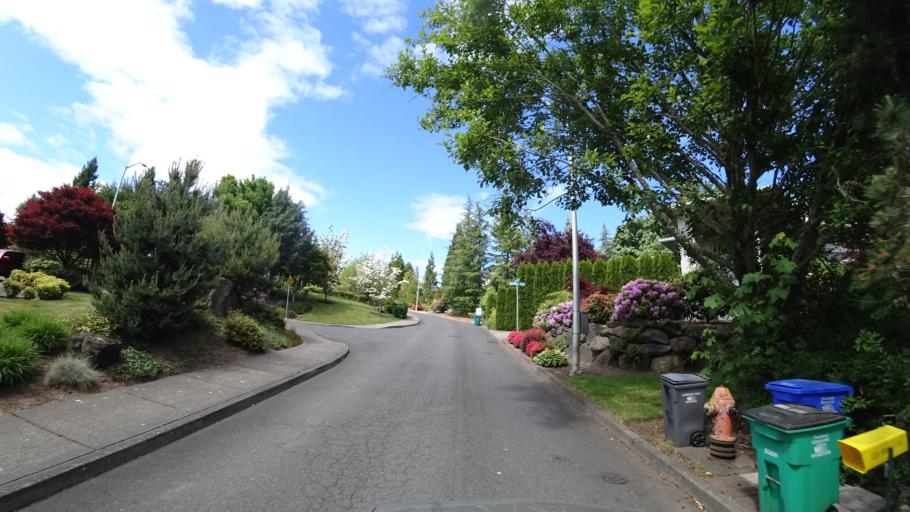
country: US
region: Oregon
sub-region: Washington County
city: Oak Hills
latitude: 45.5940
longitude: -122.8241
